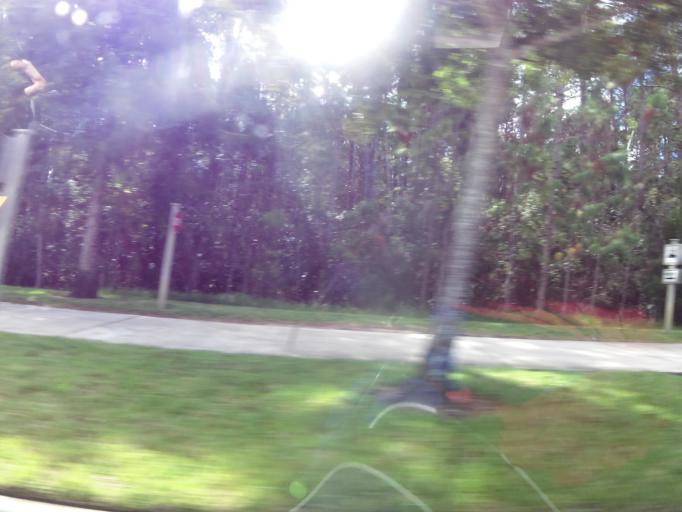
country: US
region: Florida
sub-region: Saint Johns County
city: Palm Valley
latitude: 30.1050
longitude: -81.4214
